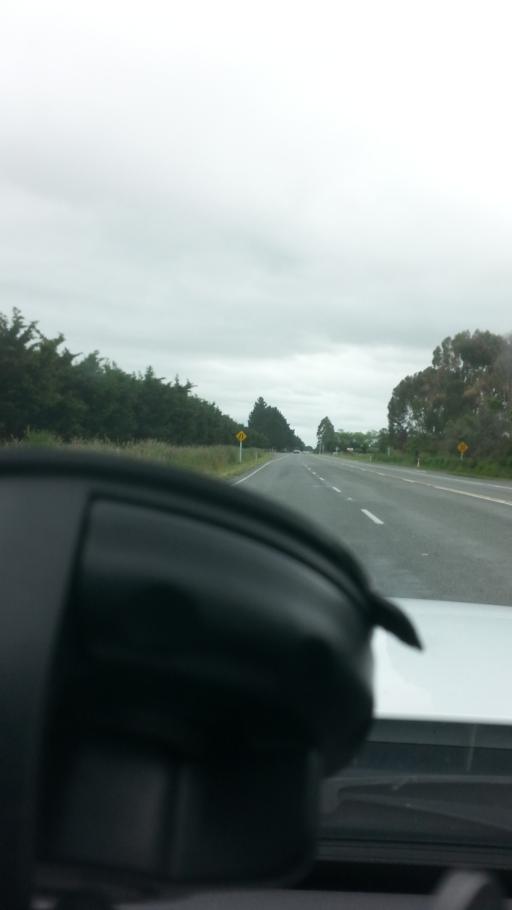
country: NZ
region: Wellington
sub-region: Masterton District
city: Masterton
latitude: -40.9697
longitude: 175.6023
